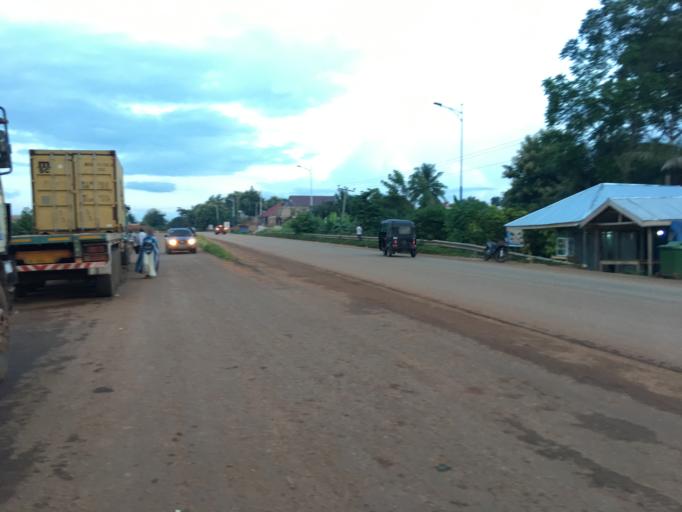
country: GH
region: Western
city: Bibiani
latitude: 6.7889
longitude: -2.5166
